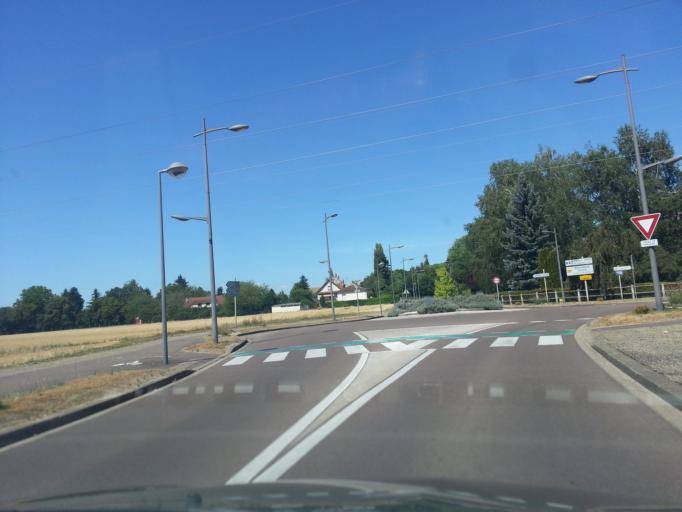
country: FR
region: Bourgogne
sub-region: Departement de Saone-et-Loire
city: Chatenoy-le-Royal
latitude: 46.7876
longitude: 4.8085
